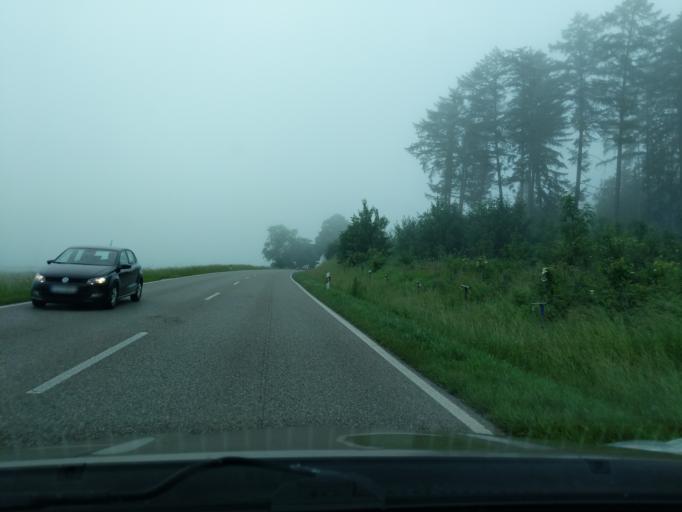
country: DE
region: Bavaria
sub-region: Swabia
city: Gessertshausen
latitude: 48.3359
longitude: 10.7479
